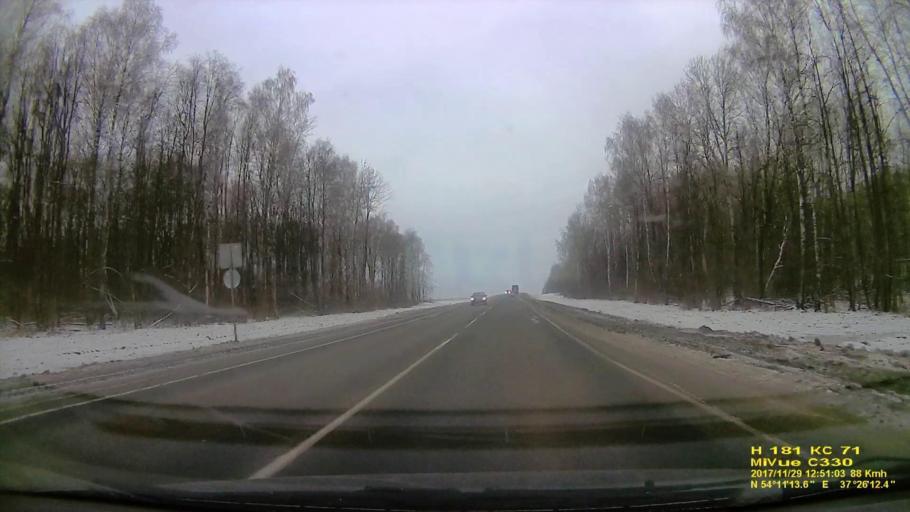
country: RU
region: Tula
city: Barsuki
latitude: 54.1871
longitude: 37.4367
